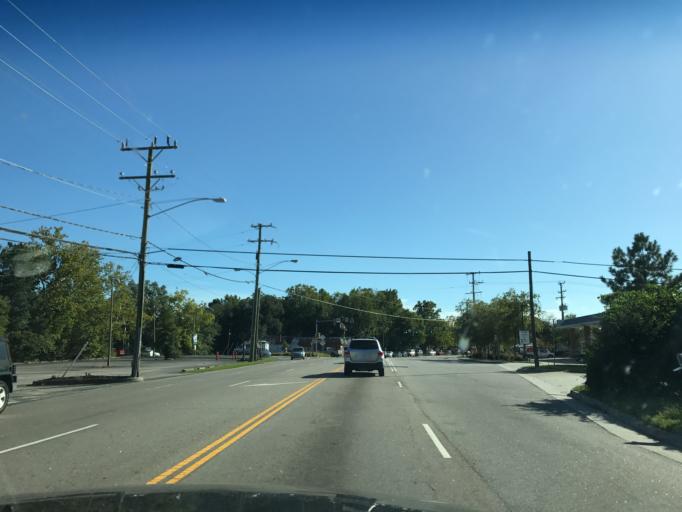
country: US
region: Virginia
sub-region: City of Portsmouth
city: Portsmouth Heights
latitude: 36.7424
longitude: -76.3453
